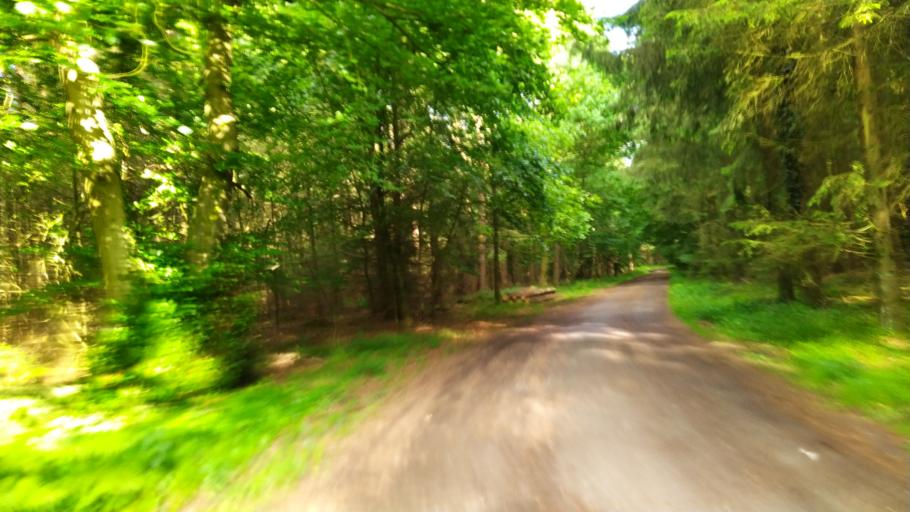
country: DE
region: Lower Saxony
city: Deinstedt
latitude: 53.4414
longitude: 9.1995
